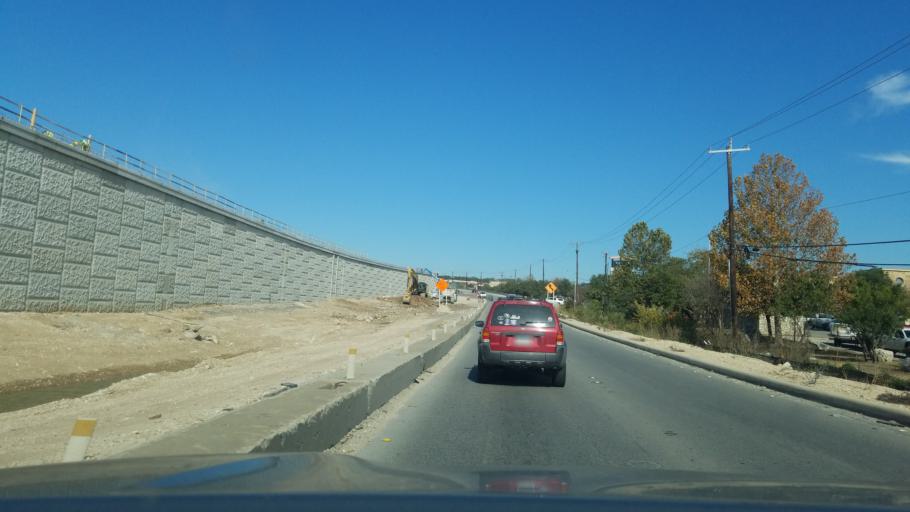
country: US
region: Texas
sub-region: Bexar County
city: Hollywood Park
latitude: 29.6499
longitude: -98.4496
